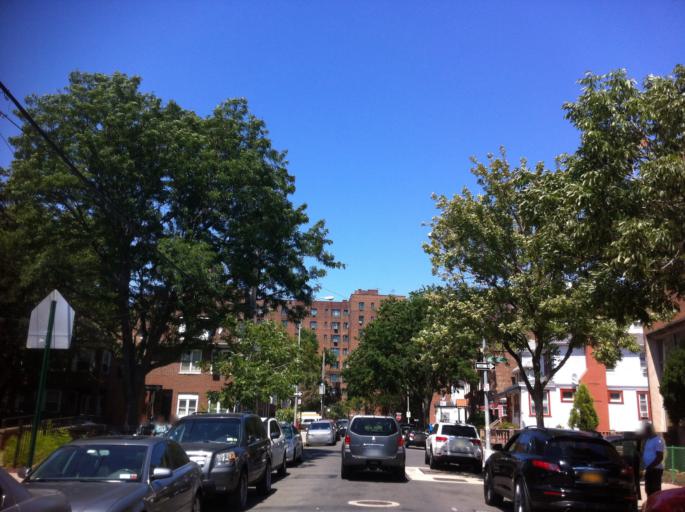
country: US
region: New York
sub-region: Bronx
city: The Bronx
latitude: 40.8332
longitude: -73.8577
